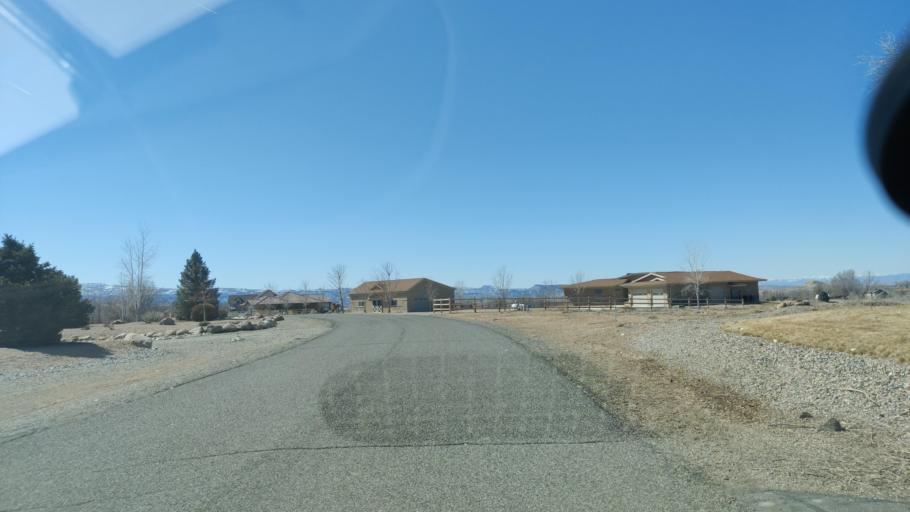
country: US
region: Colorado
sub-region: Mesa County
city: Fruita
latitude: 39.2085
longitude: -108.7108
